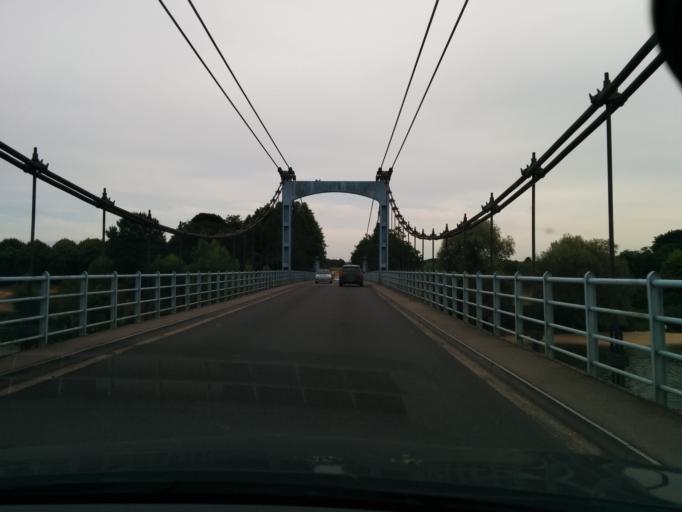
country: FR
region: Centre
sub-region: Departement du Loiret
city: Chateauneuf-sur-Loire
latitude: 47.8588
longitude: 2.2234
